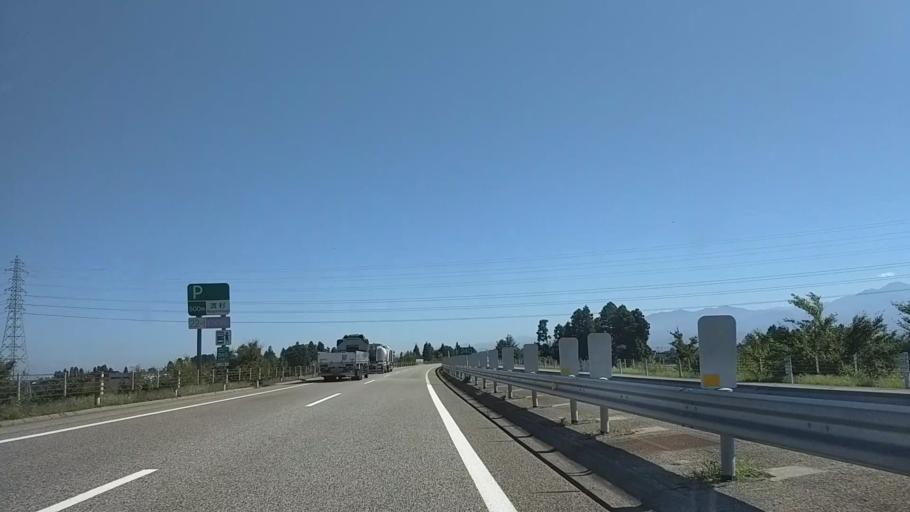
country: JP
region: Toyama
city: Toyama-shi
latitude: 36.6606
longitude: 137.2617
